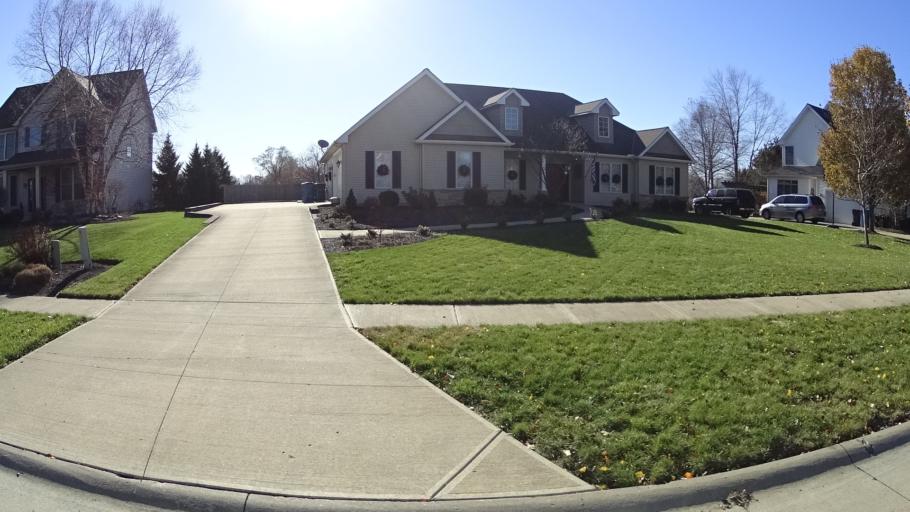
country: US
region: Ohio
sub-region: Lorain County
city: Avon Center
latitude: 41.4386
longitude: -82.0143
